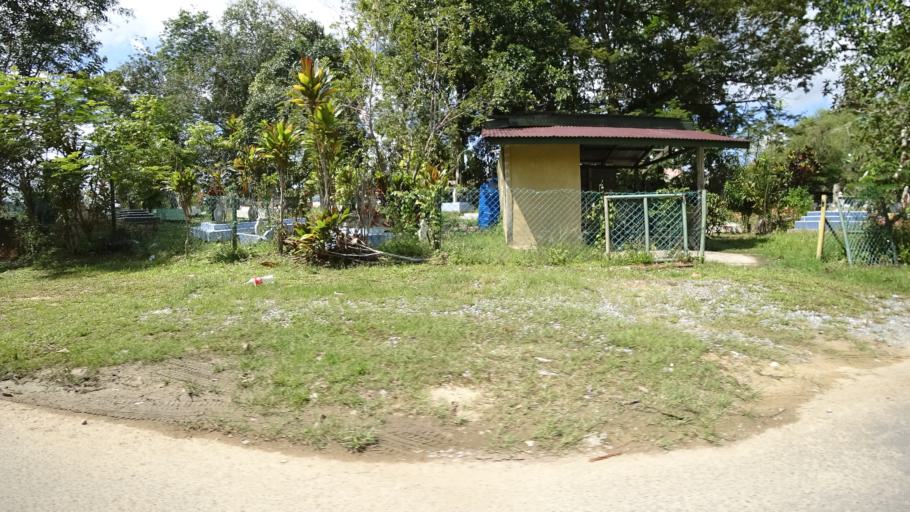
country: MY
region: Sarawak
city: Limbang
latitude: 4.7604
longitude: 115.0073
